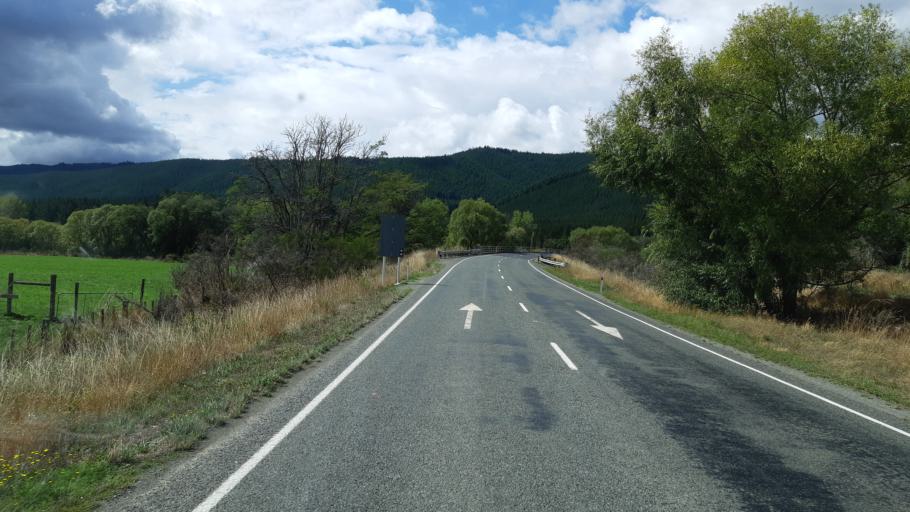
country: NZ
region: Tasman
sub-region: Tasman District
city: Wakefield
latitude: -41.4490
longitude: 172.8302
